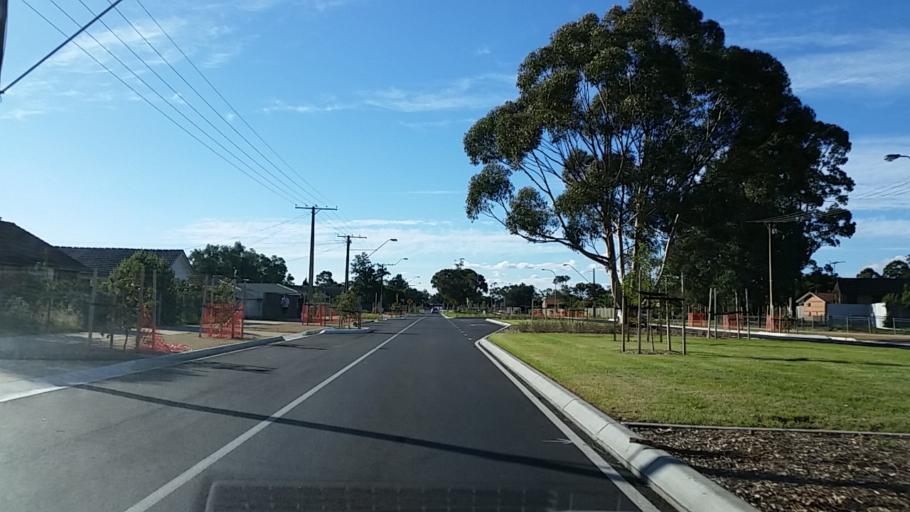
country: AU
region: South Australia
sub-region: Playford
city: Smithfield
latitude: -34.6883
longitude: 138.6699
